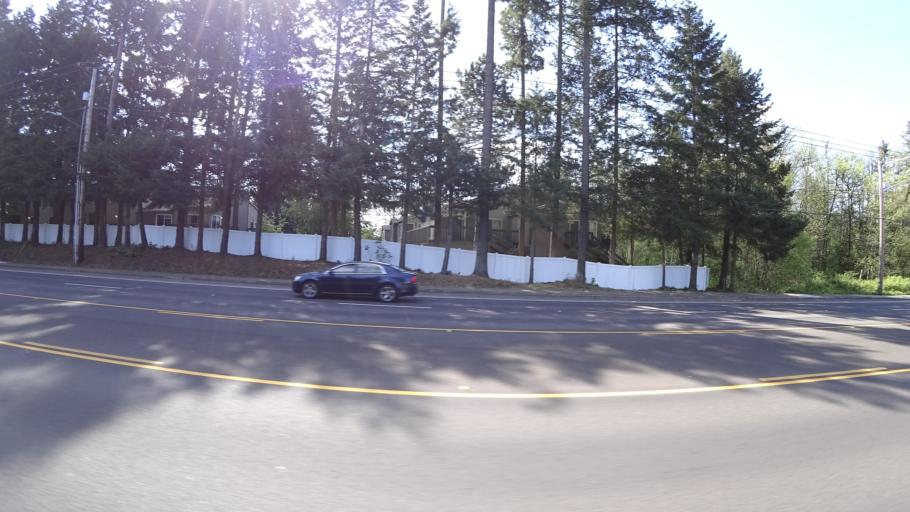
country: US
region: Oregon
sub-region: Washington County
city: King City
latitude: 45.4395
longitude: -122.8225
